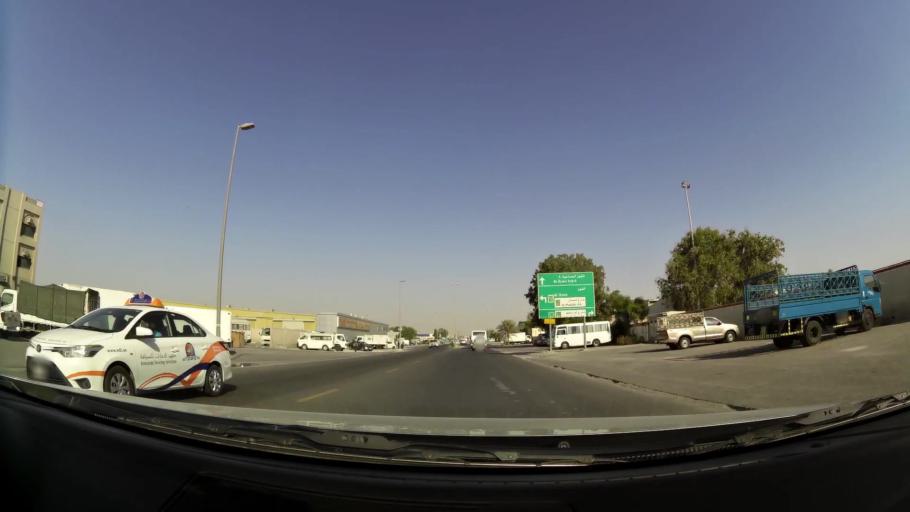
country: AE
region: Dubai
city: Dubai
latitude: 25.1217
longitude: 55.2232
